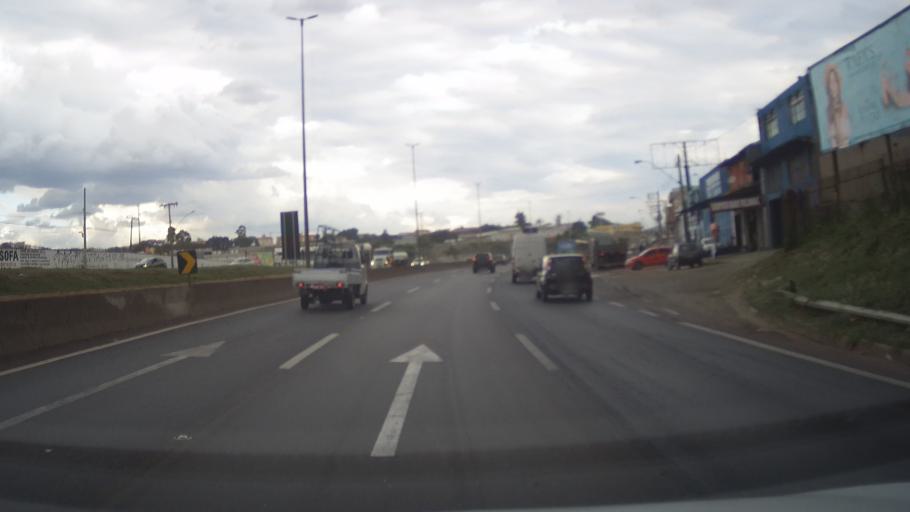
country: BR
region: Minas Gerais
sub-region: Contagem
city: Contagem
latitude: -19.9585
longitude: -44.0562
